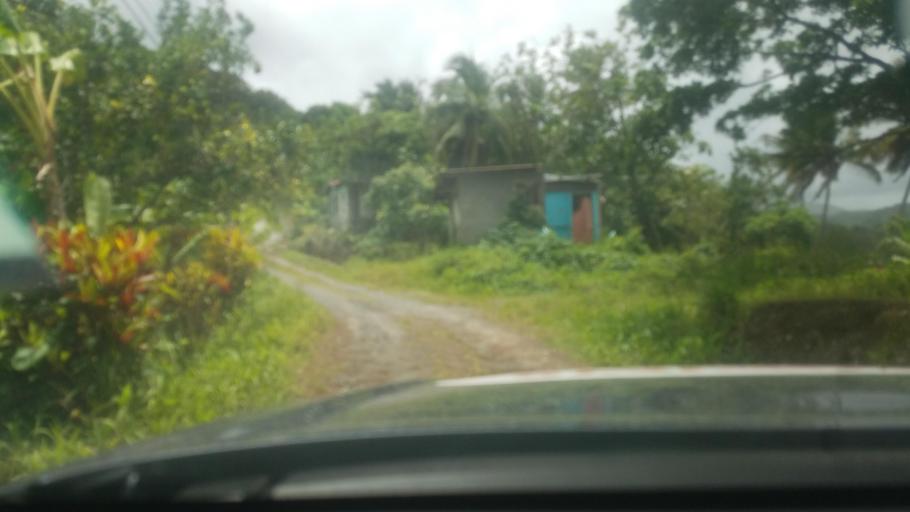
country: LC
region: Laborie Quarter
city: Laborie
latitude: 13.7825
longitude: -60.9935
